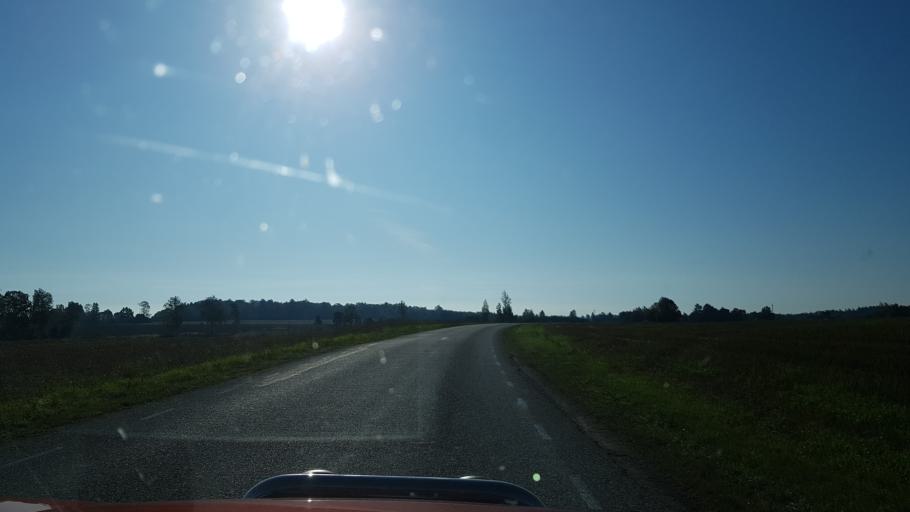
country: EE
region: Jogevamaa
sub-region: Tabivere vald
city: Tabivere
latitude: 58.6761
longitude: 26.7422
